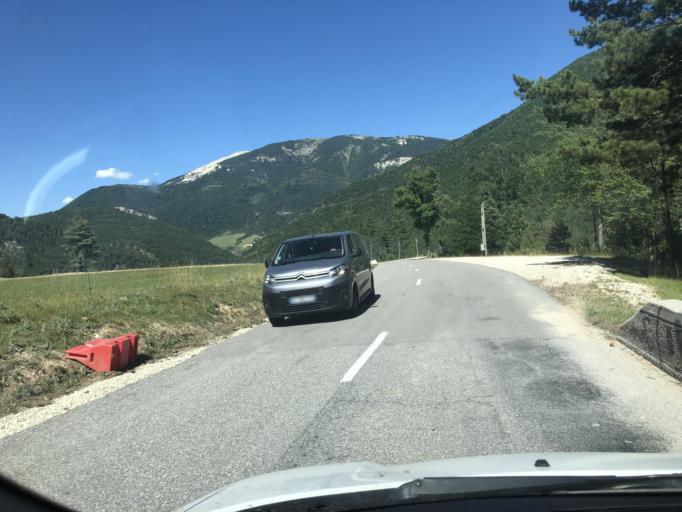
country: FR
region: Provence-Alpes-Cote d'Azur
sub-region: Departement des Alpes-de-Haute-Provence
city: Annot
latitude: 43.9960
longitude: 6.5393
